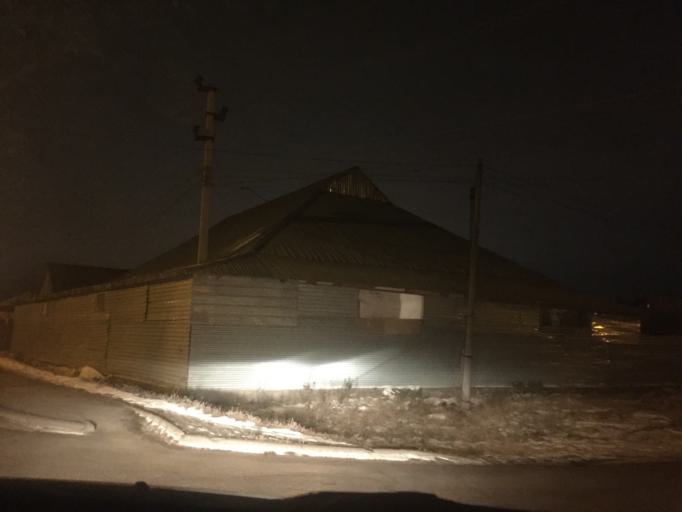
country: KZ
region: Astana Qalasy
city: Astana
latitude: 51.2151
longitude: 71.3960
